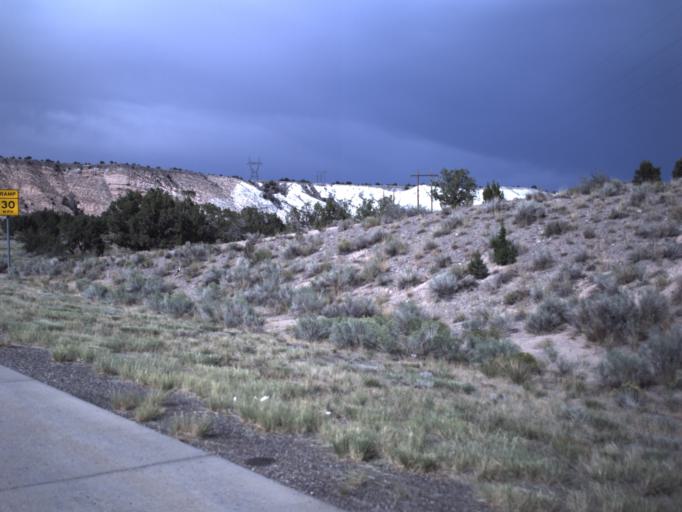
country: US
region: Utah
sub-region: Sevier County
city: Monroe
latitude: 38.6011
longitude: -112.2545
